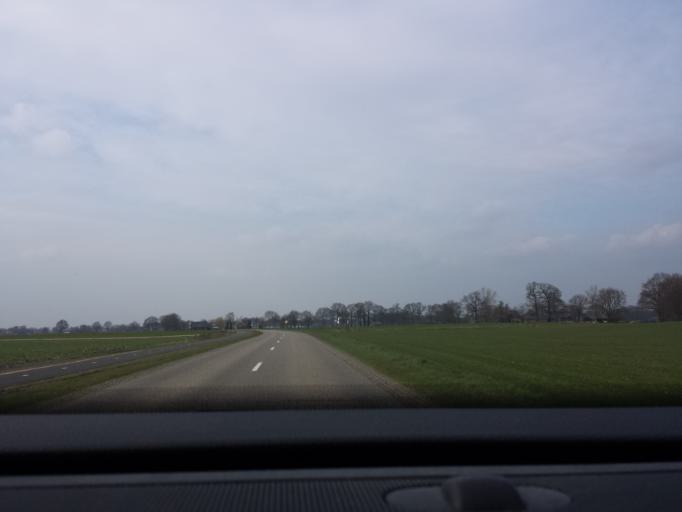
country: NL
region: Gelderland
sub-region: Gemeente Bronckhorst
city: Zelhem
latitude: 52.0249
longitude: 6.3293
